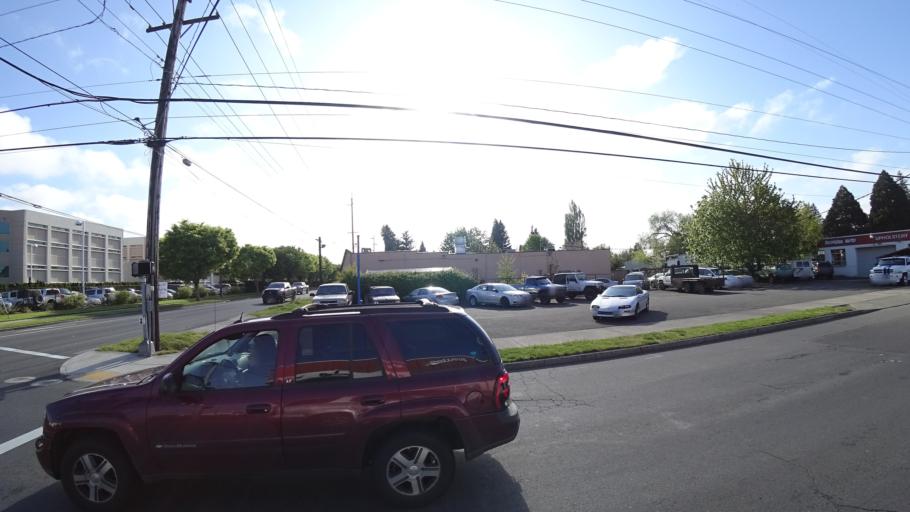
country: US
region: Oregon
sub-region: Washington County
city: Hillsboro
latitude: 45.5200
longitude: -122.9957
